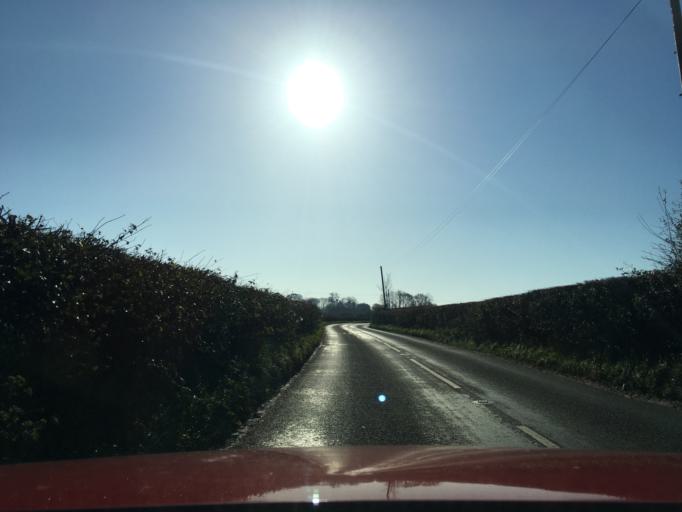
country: GB
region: England
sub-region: Somerset
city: Martock
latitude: 50.9927
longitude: -2.7679
